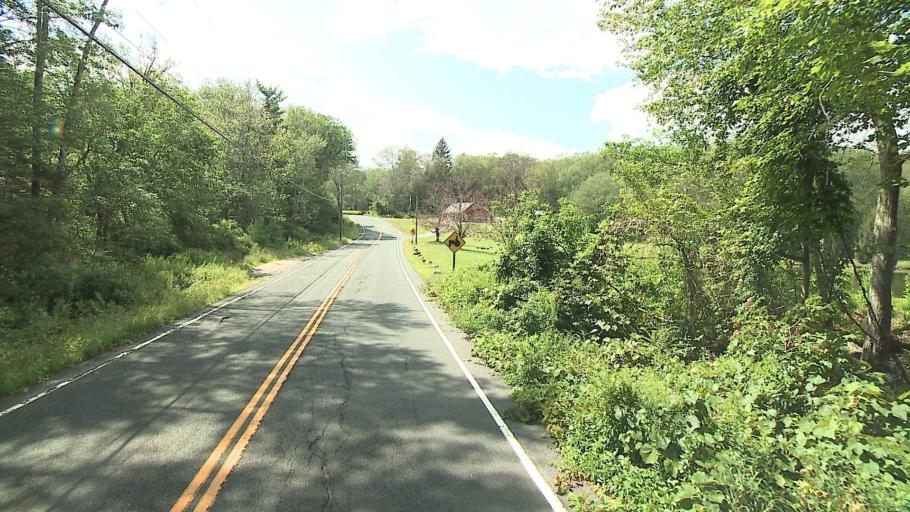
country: US
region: Connecticut
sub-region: Tolland County
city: Stafford Springs
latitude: 41.9486
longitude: -72.3305
